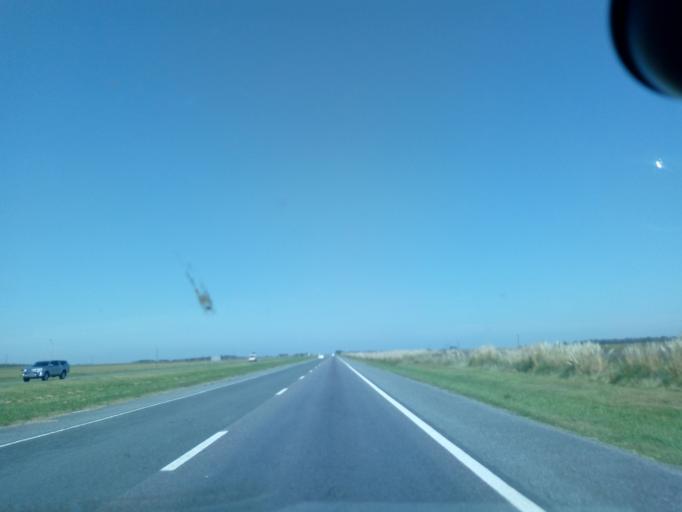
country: AR
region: Buenos Aires
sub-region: Partido de General Guido
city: General Guido
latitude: -36.7106
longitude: -57.7979
